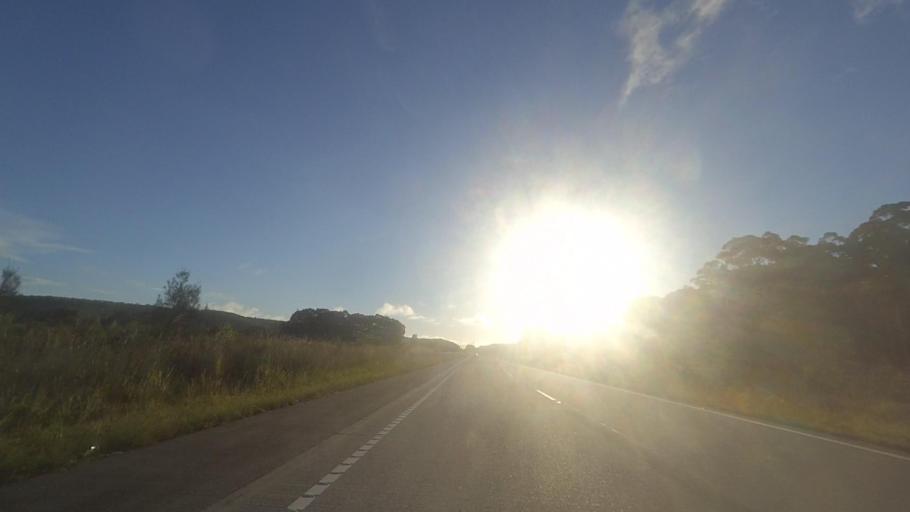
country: AU
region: New South Wales
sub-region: Great Lakes
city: Bulahdelah
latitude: -32.5248
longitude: 152.1965
